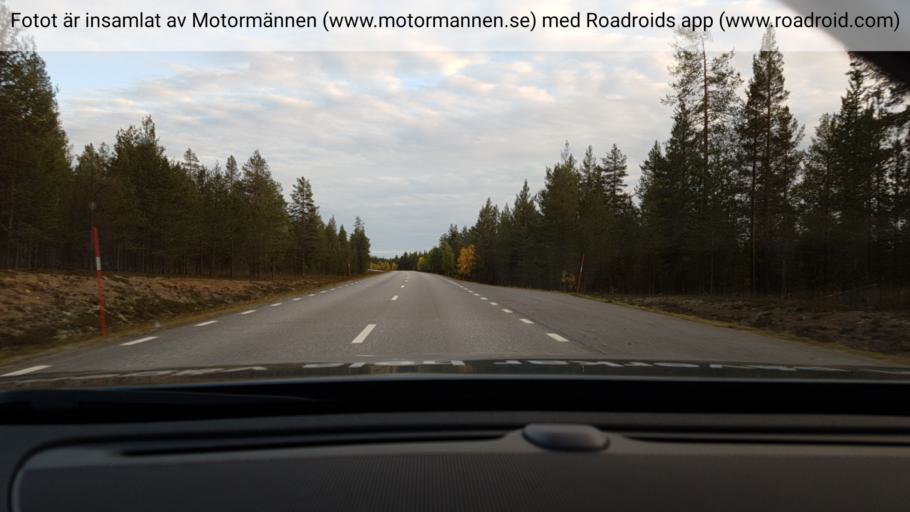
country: SE
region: Norrbotten
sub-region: Jokkmokks Kommun
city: Jokkmokk
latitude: 66.3969
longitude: 19.6968
